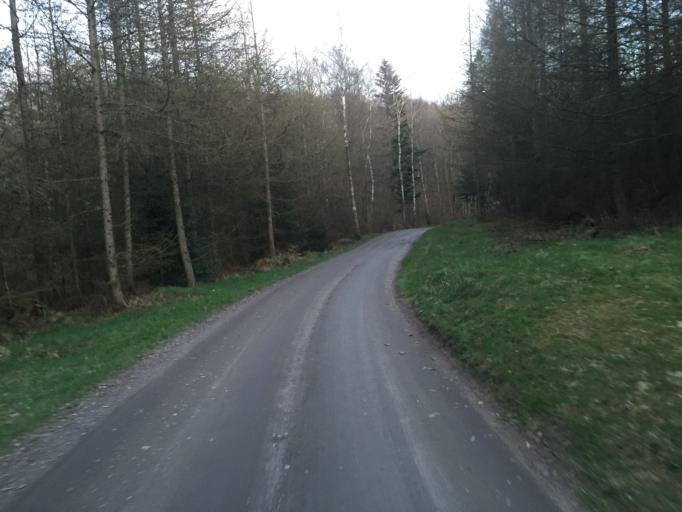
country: SE
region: Skane
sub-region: Lunds Kommun
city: Veberod
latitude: 55.6129
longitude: 13.5110
